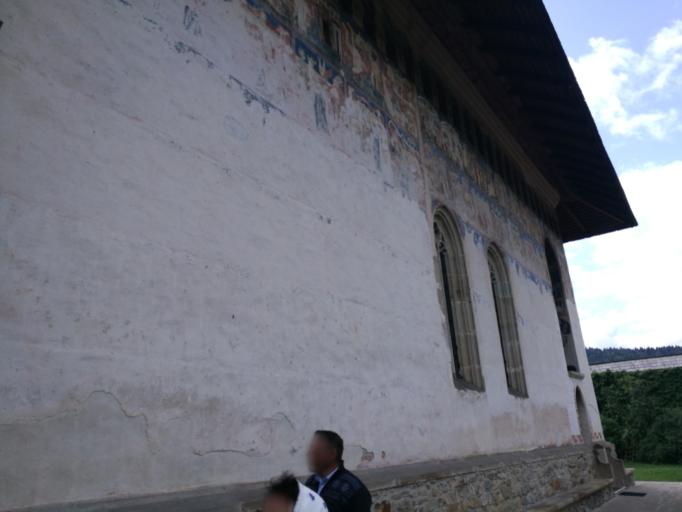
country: RO
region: Suceava
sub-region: Comuna Vatra Moldovitei
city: Vatra Moldovitei
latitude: 47.6571
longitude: 25.5712
